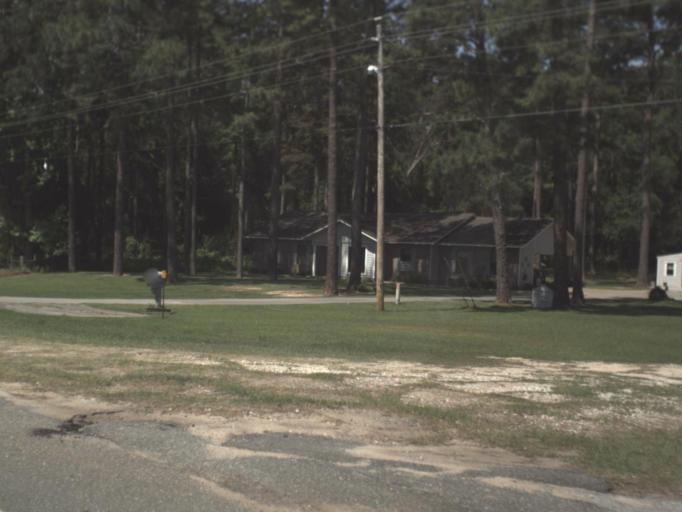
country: US
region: Florida
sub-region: Jackson County
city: Marianna
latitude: 30.8107
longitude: -85.2115
